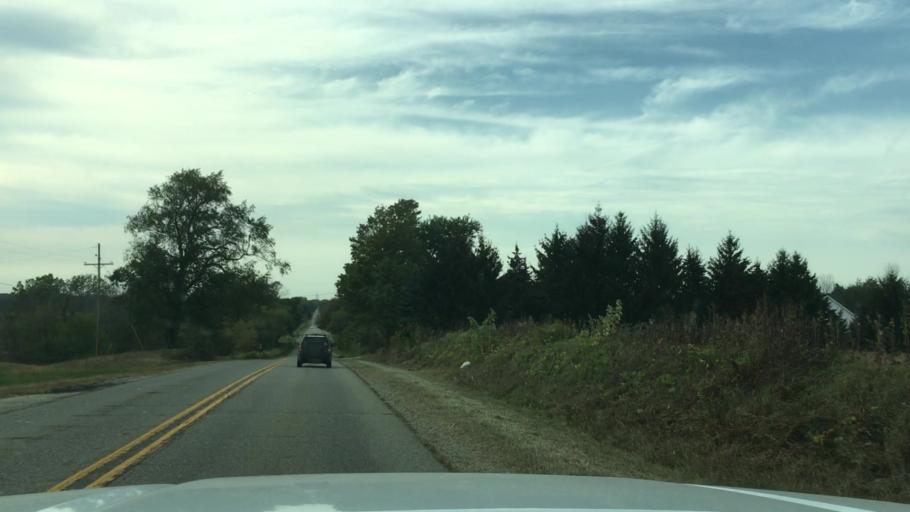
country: US
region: Michigan
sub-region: Ottawa County
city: Hudsonville
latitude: 42.7821
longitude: -85.8535
